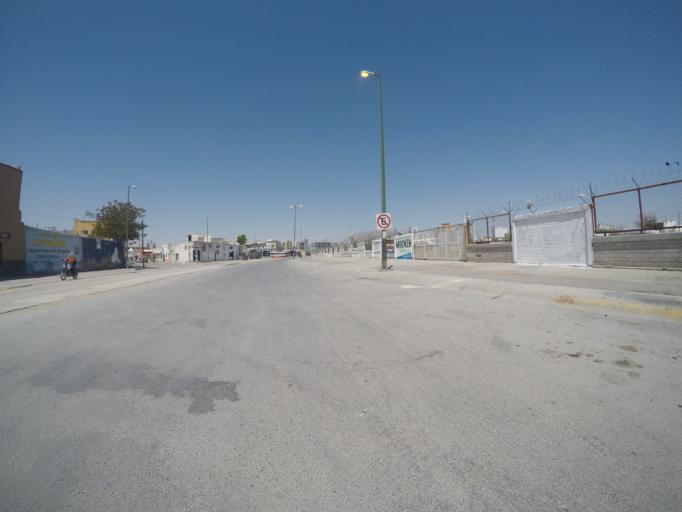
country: MX
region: Chihuahua
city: Ciudad Juarez
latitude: 31.7346
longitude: -106.4819
